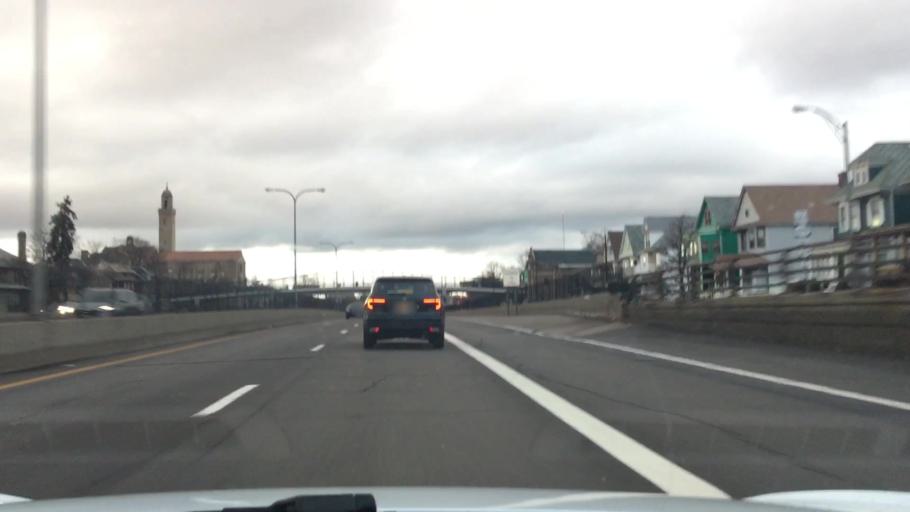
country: US
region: New York
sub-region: Erie County
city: Buffalo
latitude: 42.9168
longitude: -78.8433
